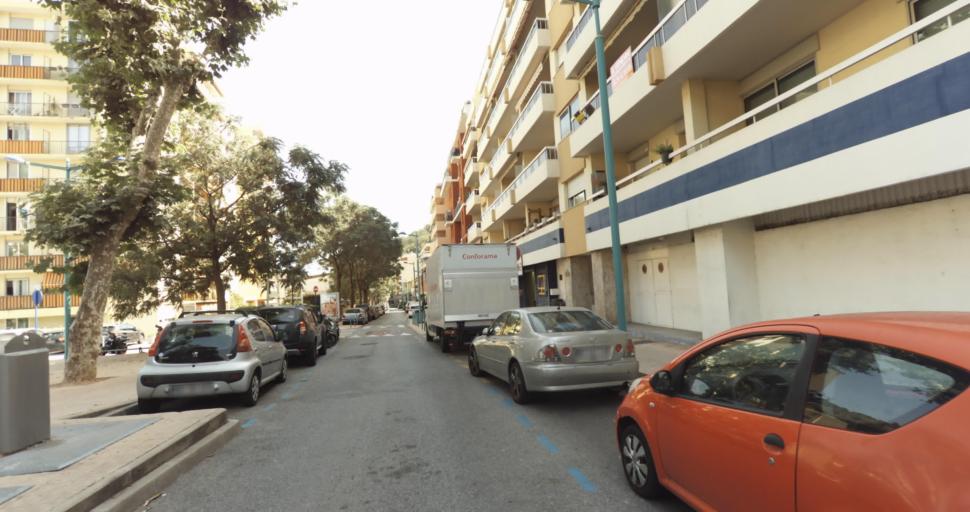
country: FR
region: Provence-Alpes-Cote d'Azur
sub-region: Departement des Alpes-Maritimes
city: Menton
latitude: 43.7903
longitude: 7.4920
